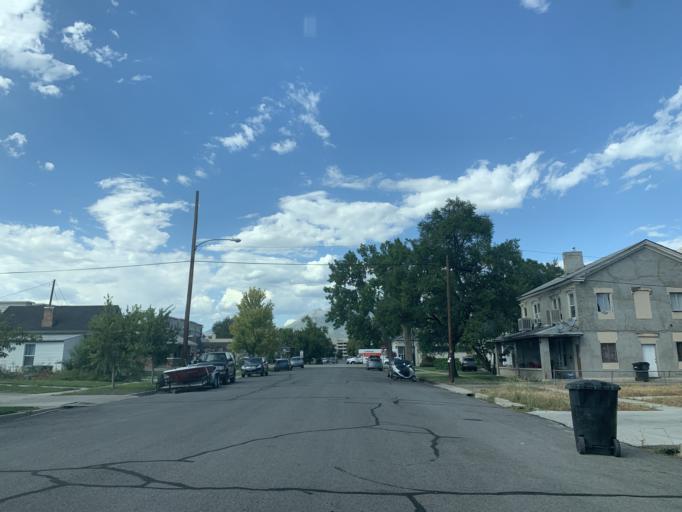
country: US
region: Utah
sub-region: Utah County
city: Provo
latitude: 40.2288
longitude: -111.6568
